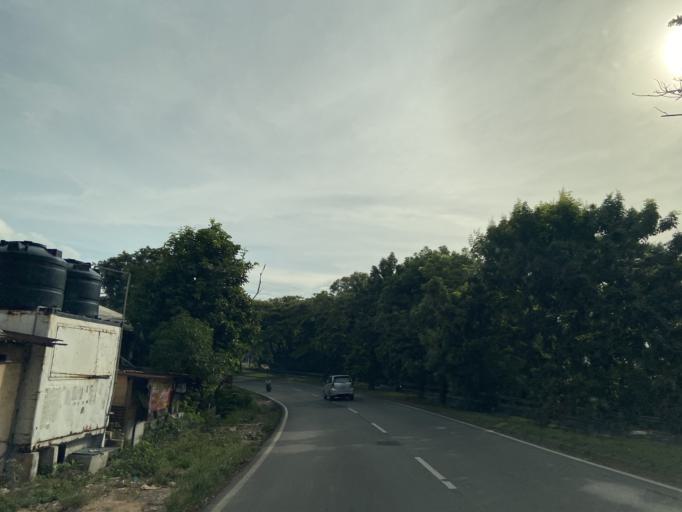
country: SG
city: Singapore
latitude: 1.1479
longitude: 104.0229
